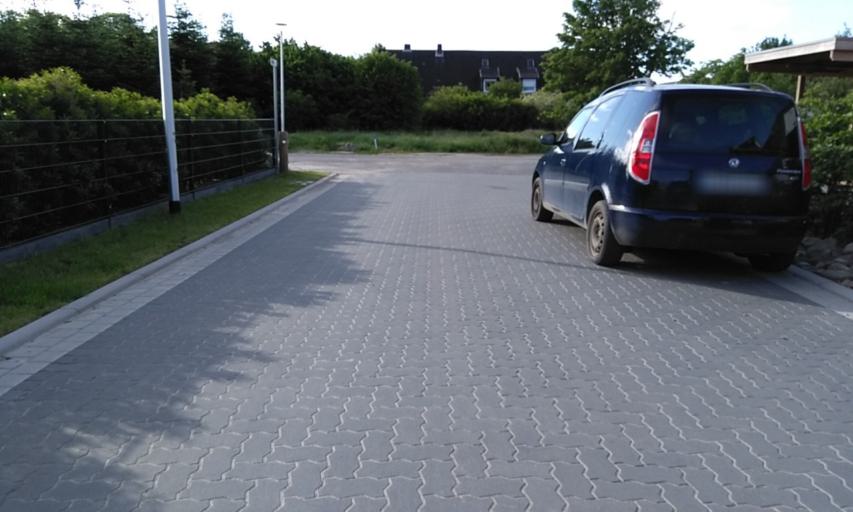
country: DE
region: Lower Saxony
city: Apensen
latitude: 53.4393
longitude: 9.6221
